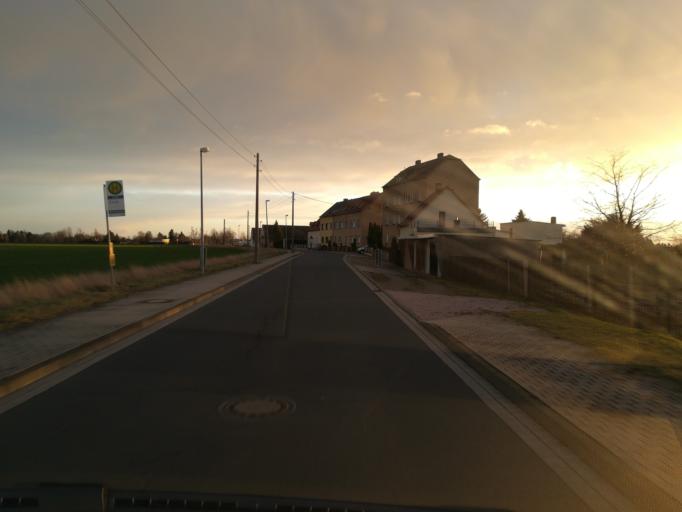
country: DE
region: Saxony
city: Wiedemar
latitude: 51.5070
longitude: 12.2275
